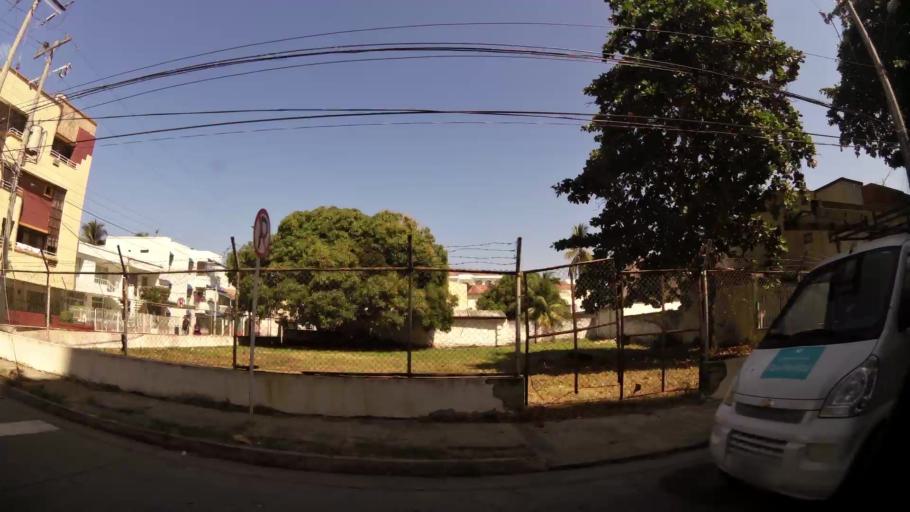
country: CO
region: Bolivar
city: Cartagena
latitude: 10.4450
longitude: -75.5213
